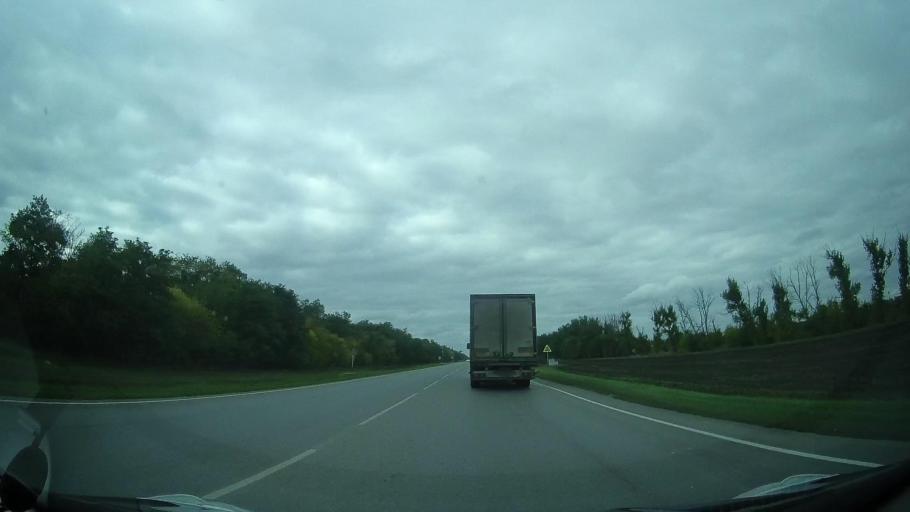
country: RU
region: Rostov
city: Yegorlykskaya
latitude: 46.6246
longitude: 40.5936
